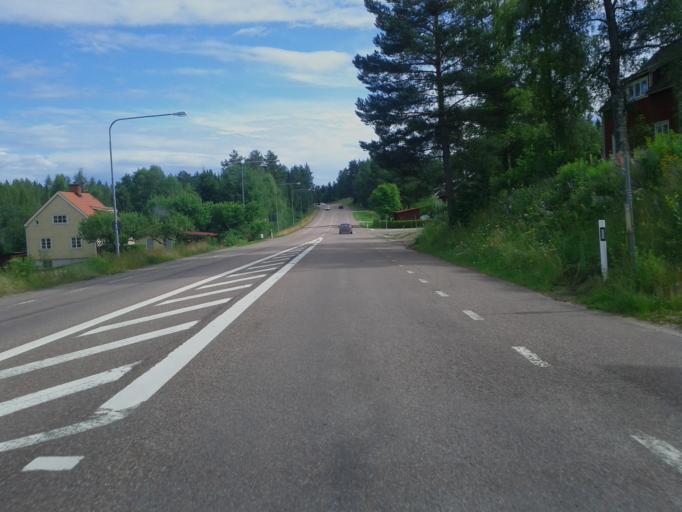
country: SE
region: Dalarna
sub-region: Faluns Kommun
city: Bjursas
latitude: 60.7330
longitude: 15.4390
